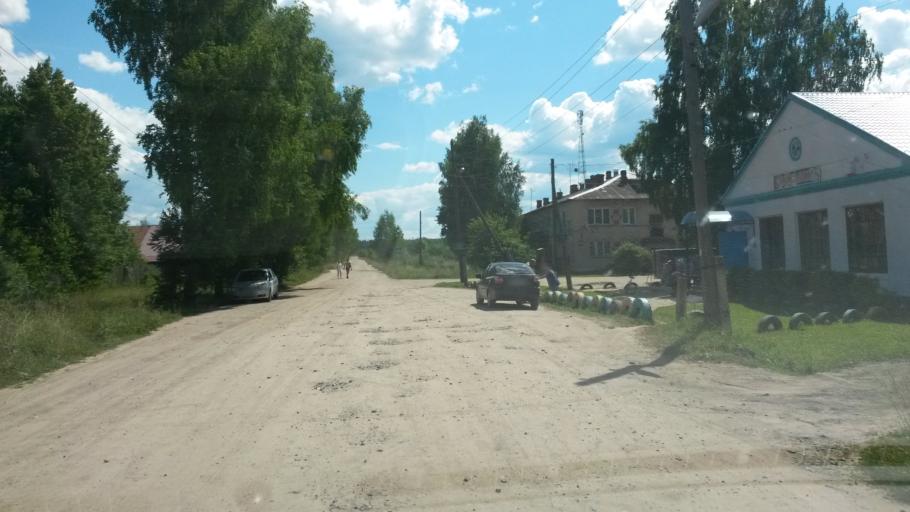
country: RU
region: Ivanovo
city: Zarechnyy
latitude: 57.4983
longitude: 42.3330
